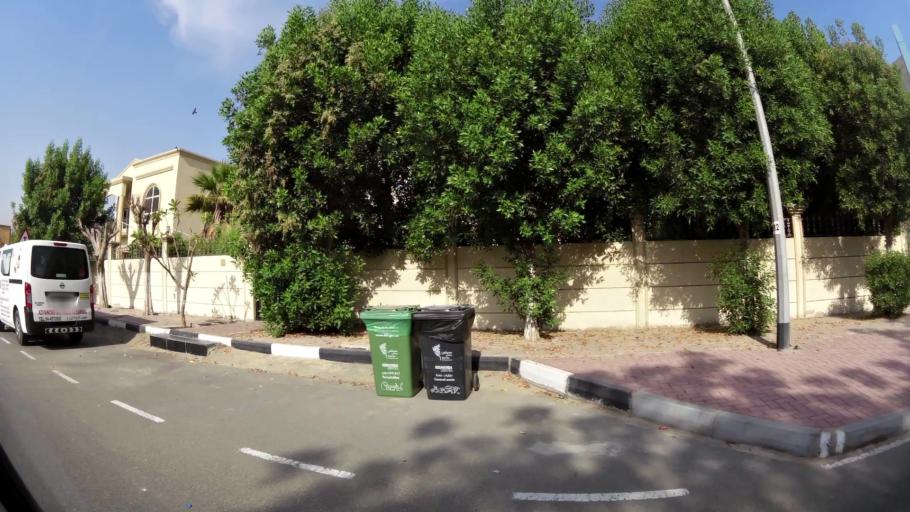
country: AE
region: Ash Shariqah
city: Sharjah
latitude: 25.2411
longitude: 55.4091
